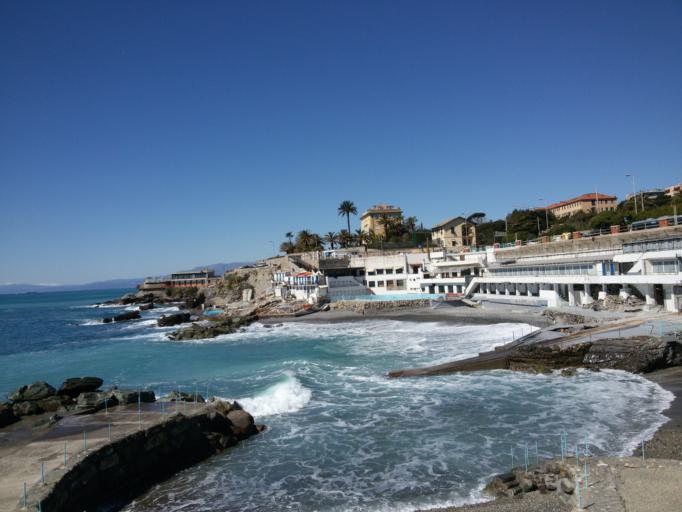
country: IT
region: Liguria
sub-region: Provincia di Genova
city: Bogliasco
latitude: 44.3853
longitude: 9.0083
